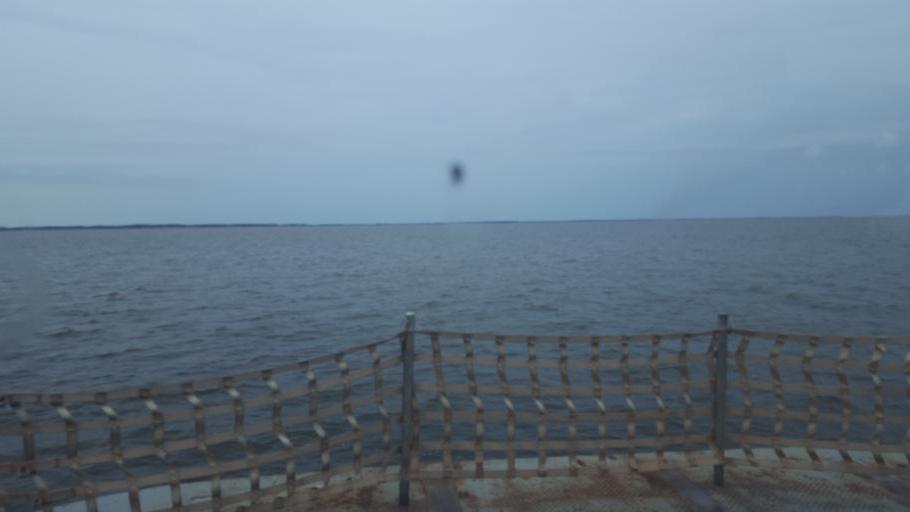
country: US
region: North Carolina
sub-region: Currituck County
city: Currituck
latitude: 36.4562
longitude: -75.9871
